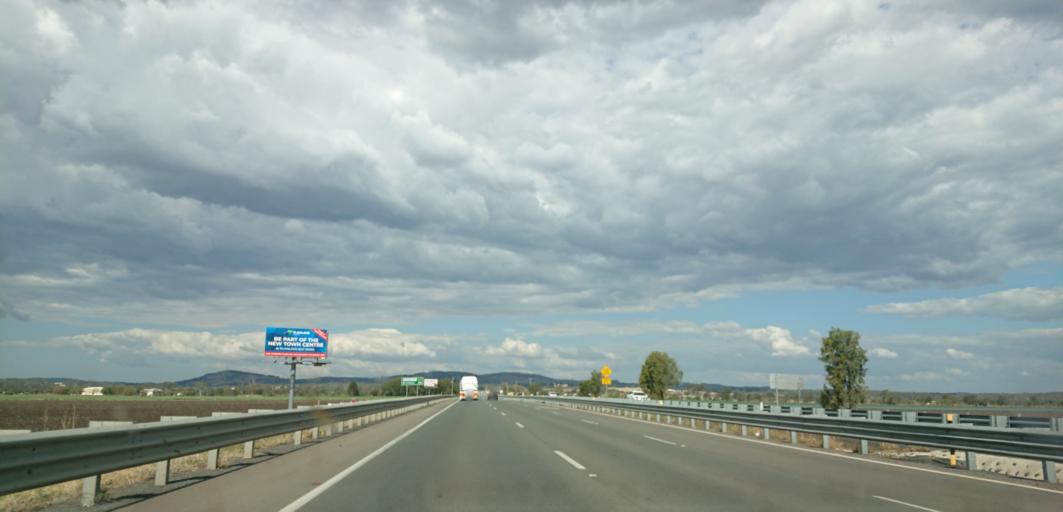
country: AU
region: Queensland
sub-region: Lockyer Valley
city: Gatton
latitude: -27.5449
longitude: 152.3798
